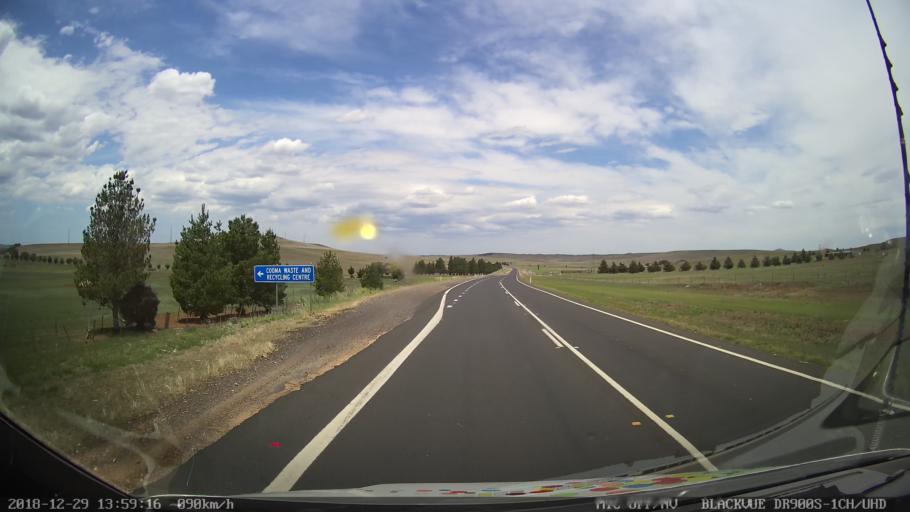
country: AU
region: New South Wales
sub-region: Cooma-Monaro
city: Cooma
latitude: -36.2504
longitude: 149.1478
